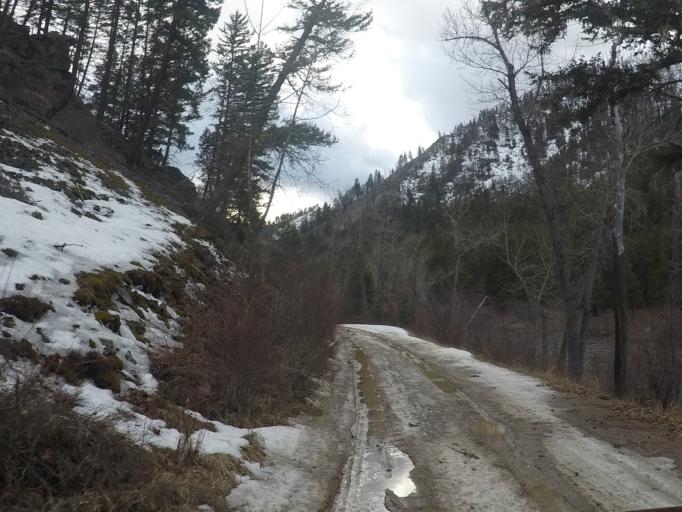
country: US
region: Montana
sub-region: Missoula County
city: Clinton
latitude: 46.5688
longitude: -113.6982
